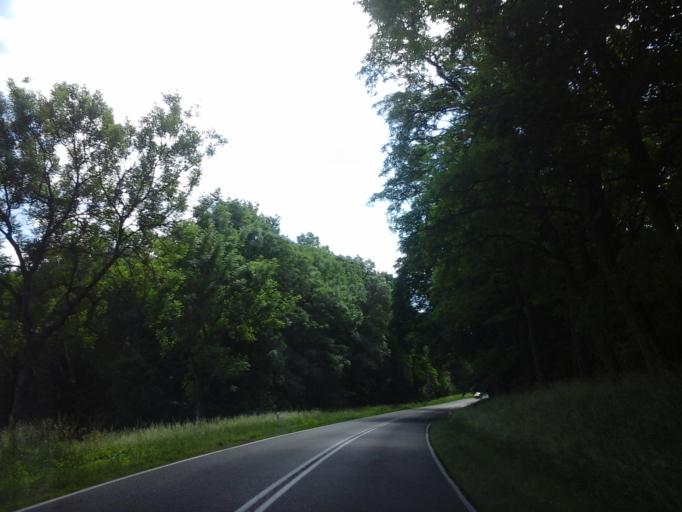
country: PL
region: West Pomeranian Voivodeship
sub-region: Powiat stargardzki
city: Suchan
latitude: 53.2091
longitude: 15.3214
